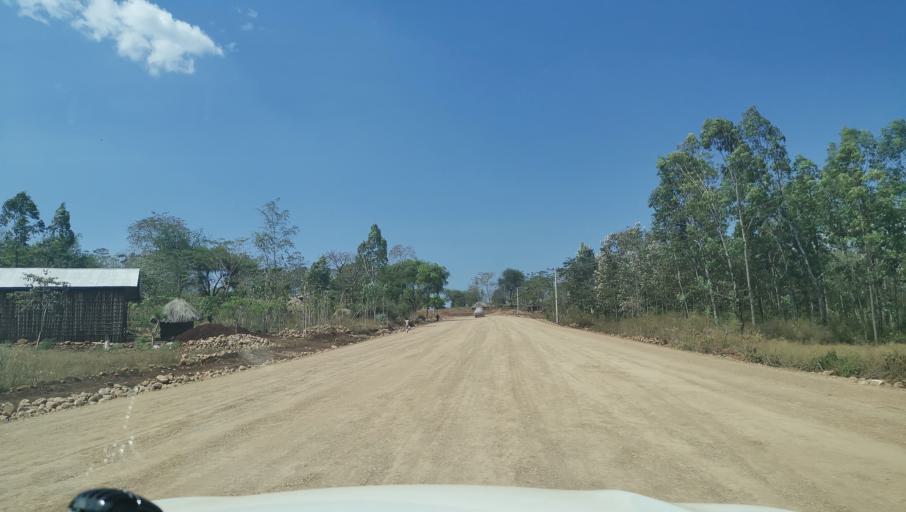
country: ET
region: Southern Nations, Nationalities, and People's Region
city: Arba Minch'
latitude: 6.3367
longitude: 37.2934
